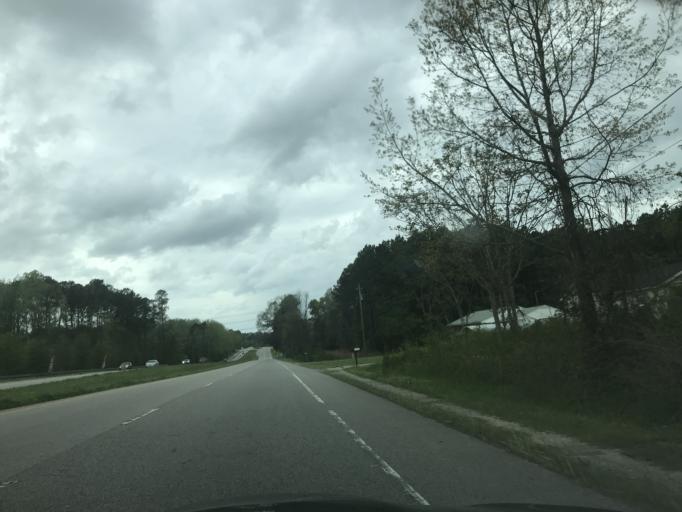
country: US
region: North Carolina
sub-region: Wake County
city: Knightdale
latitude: 35.8046
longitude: -78.4463
